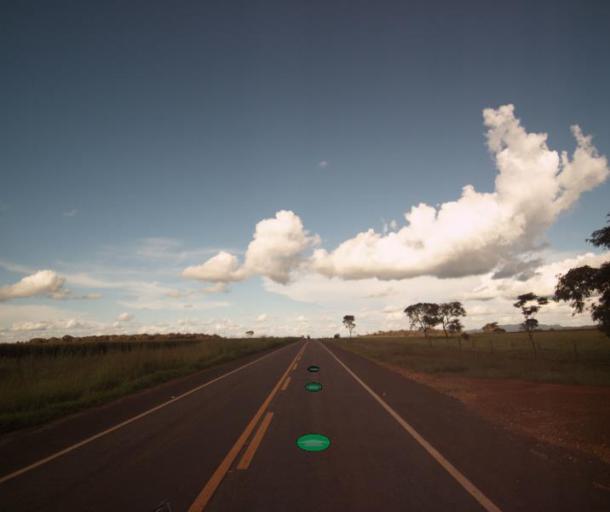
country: BR
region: Goias
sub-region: Itaberai
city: Itaberai
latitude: -15.9852
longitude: -49.7021
